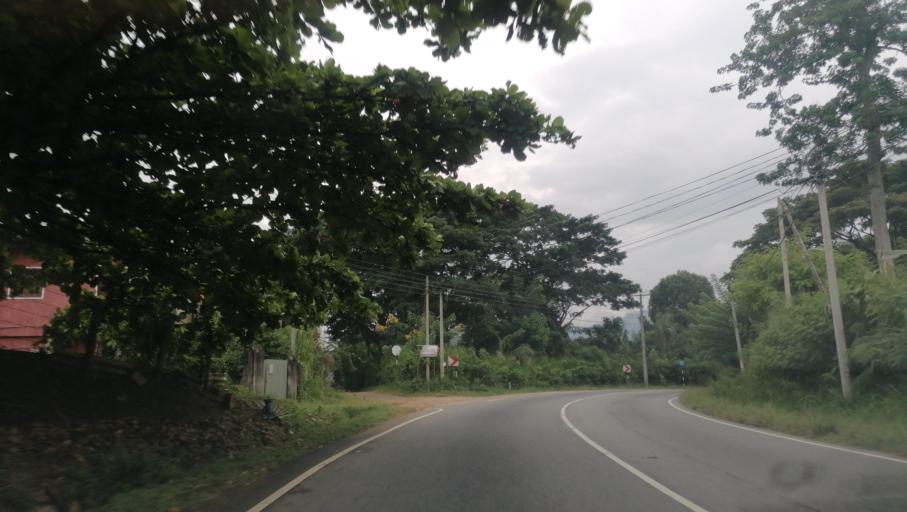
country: LK
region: Central
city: Kandy
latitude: 7.2500
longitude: 80.7316
